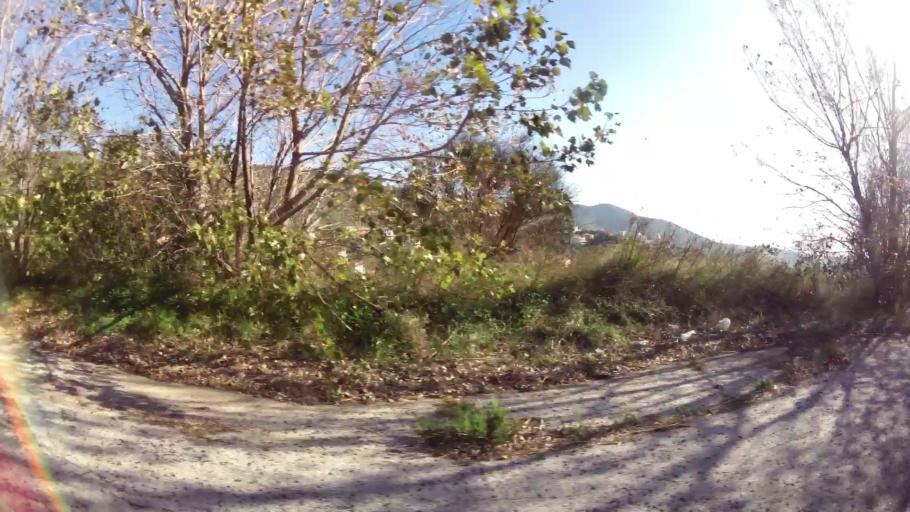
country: GR
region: Attica
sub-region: Nomarchia Anatolikis Attikis
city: Dhrafi
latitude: 38.0425
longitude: 23.8938
